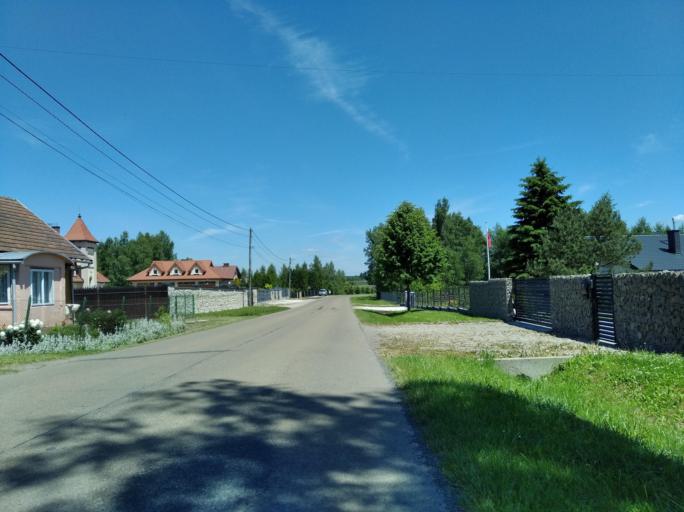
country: PL
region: Subcarpathian Voivodeship
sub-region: Powiat jasielski
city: Tarnowiec
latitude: 49.7245
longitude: 21.5641
